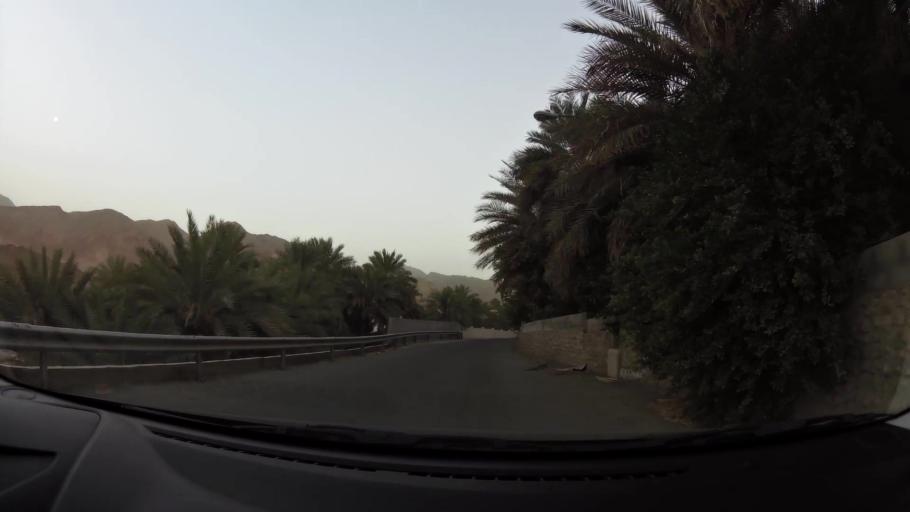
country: OM
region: Muhafazat Masqat
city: Bawshar
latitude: 23.4832
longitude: 58.3283
